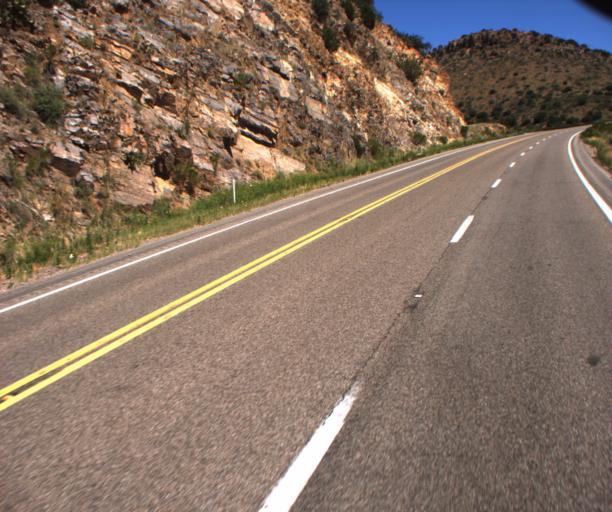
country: US
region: Arizona
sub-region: Gila County
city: Globe
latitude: 33.5052
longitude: -110.7065
